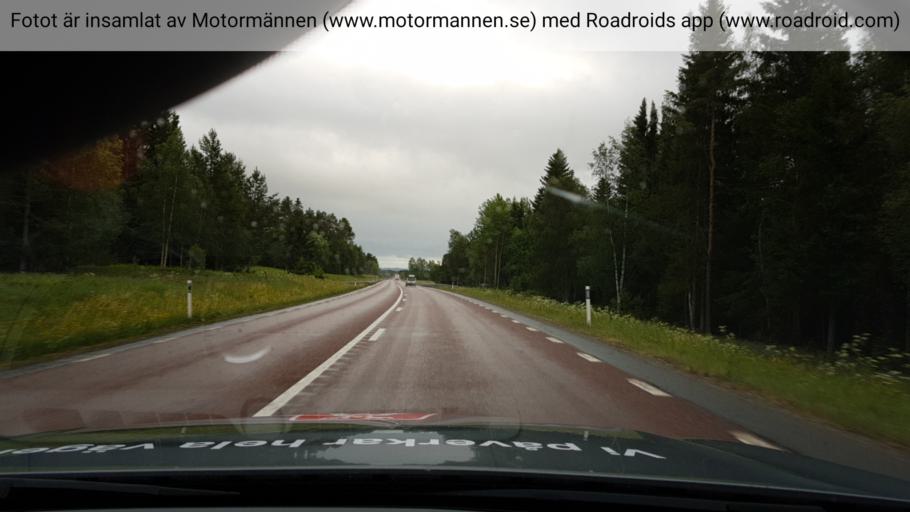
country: SE
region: Jaemtland
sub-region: Bergs Kommun
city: Hoverberg
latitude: 62.9802
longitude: 14.5675
